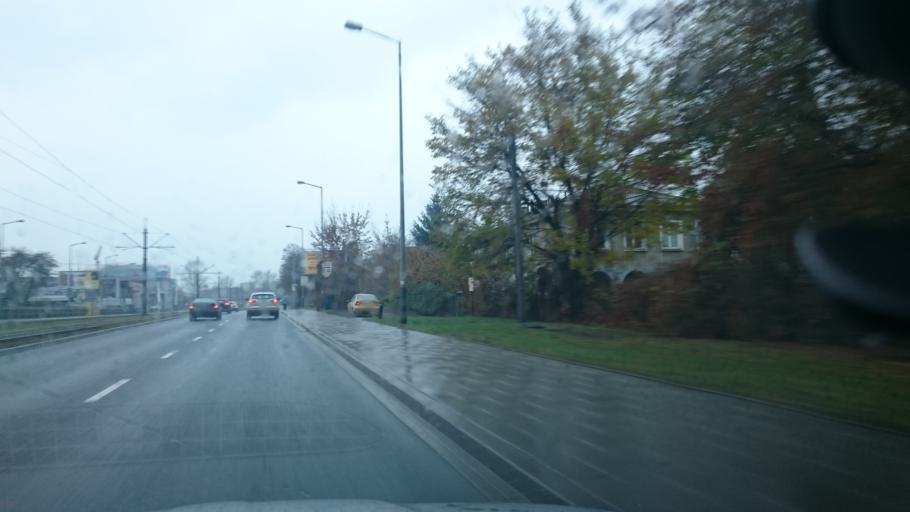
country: PL
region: Lesser Poland Voivodeship
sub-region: Krakow
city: Krakow
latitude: 50.0466
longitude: 19.9717
